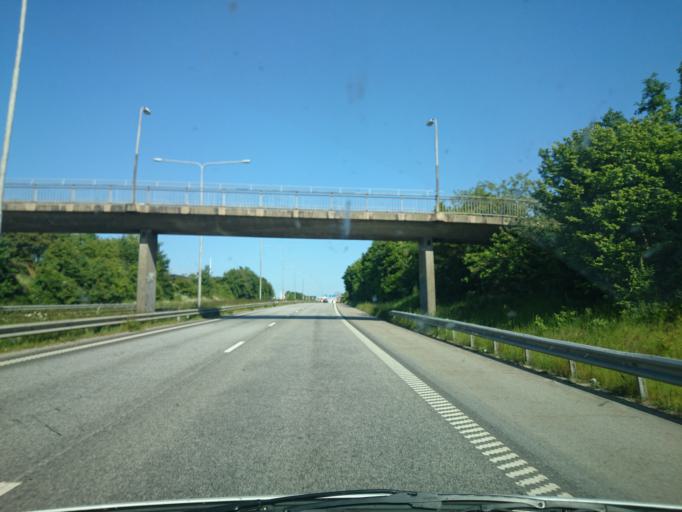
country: SE
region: Skane
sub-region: Lunds Kommun
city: Lund
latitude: 55.7209
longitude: 13.1944
